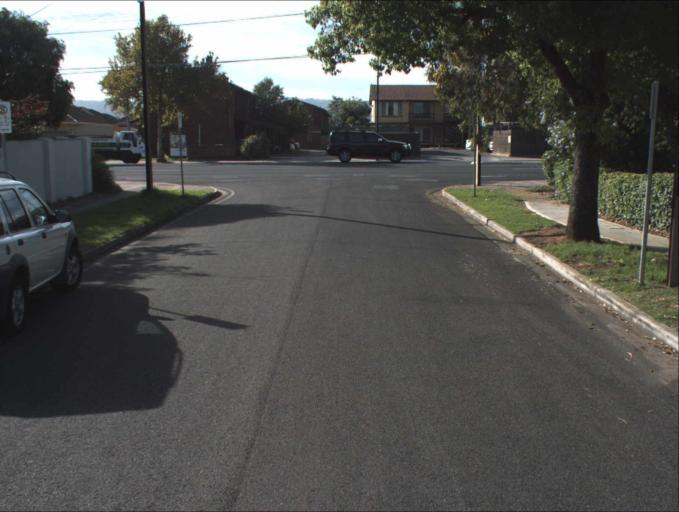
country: AU
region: South Australia
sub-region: Port Adelaide Enfield
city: Klemzig
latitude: -34.8786
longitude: 138.6267
